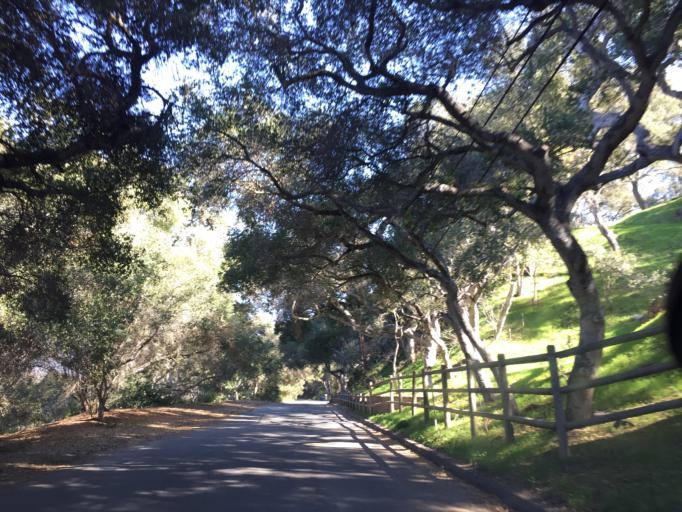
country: US
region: California
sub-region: Santa Barbara County
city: Goleta
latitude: 34.4322
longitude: -119.7781
